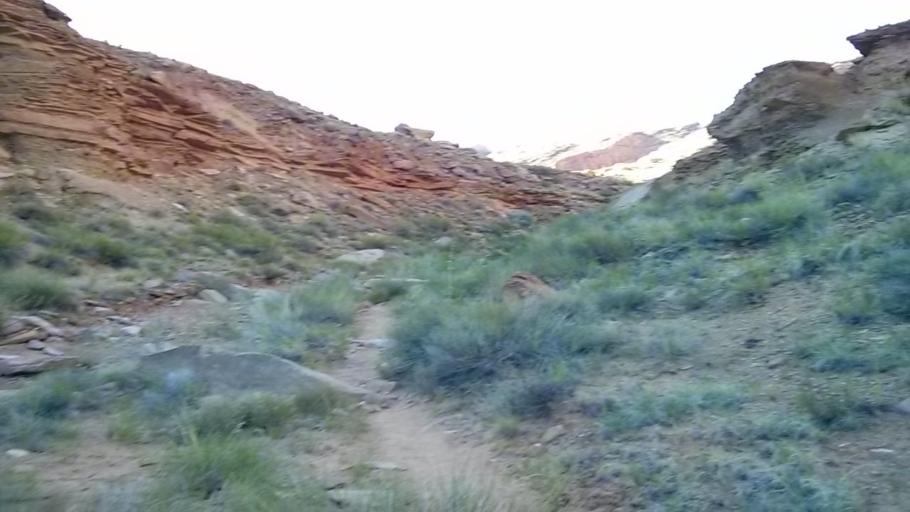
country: US
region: Utah
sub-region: Grand County
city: Moab
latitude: 38.4385
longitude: -109.9560
